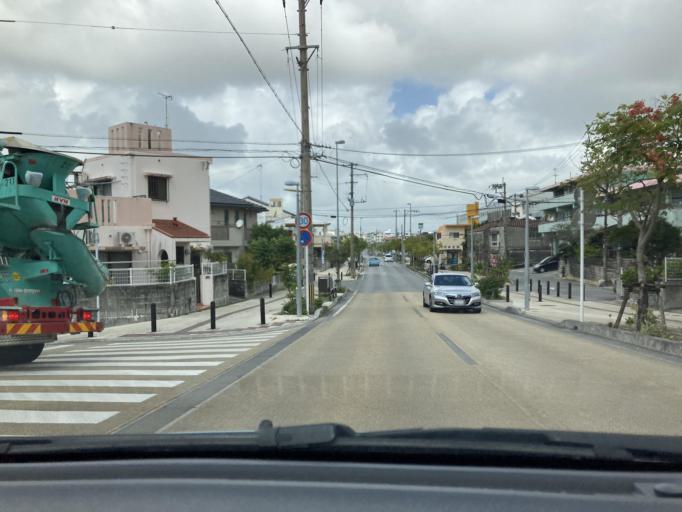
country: JP
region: Okinawa
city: Ginowan
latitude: 26.2292
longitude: 127.7323
